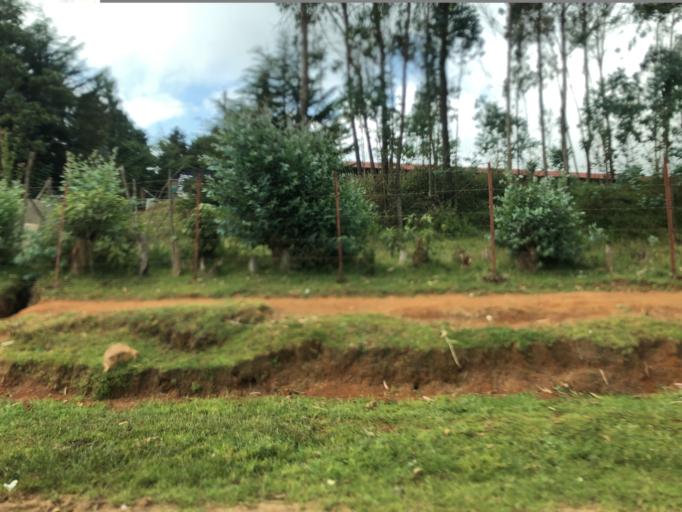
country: ET
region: Southern Nations, Nationalities, and People's Region
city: Arba Minch'
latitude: 6.1988
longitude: 37.5726
